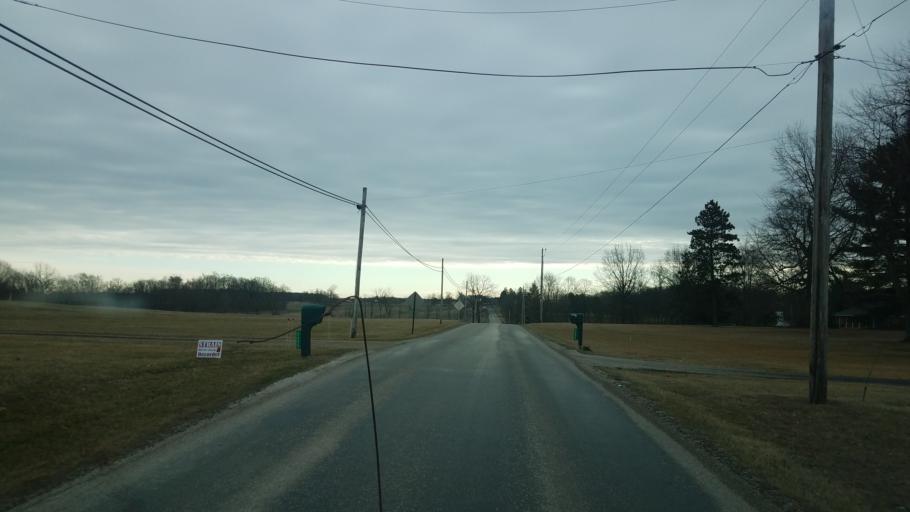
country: US
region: Ohio
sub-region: Morrow County
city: Mount Gilead
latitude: 40.5166
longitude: -82.8338
